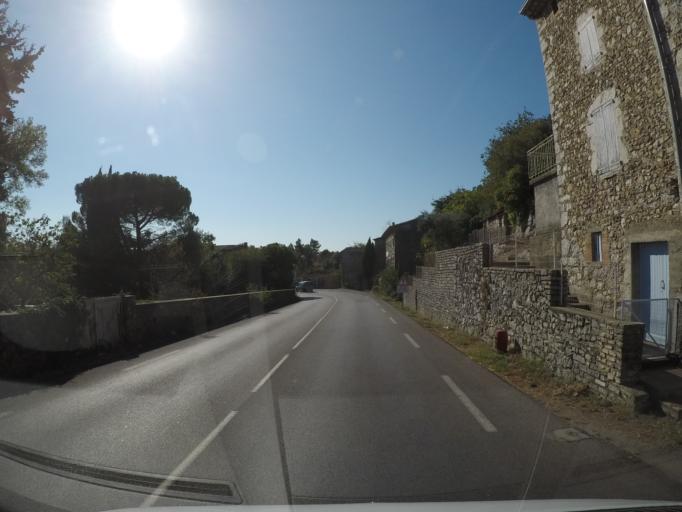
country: FR
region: Languedoc-Roussillon
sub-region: Departement du Gard
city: Boisset-et-Gaujac
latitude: 44.0378
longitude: 4.0006
